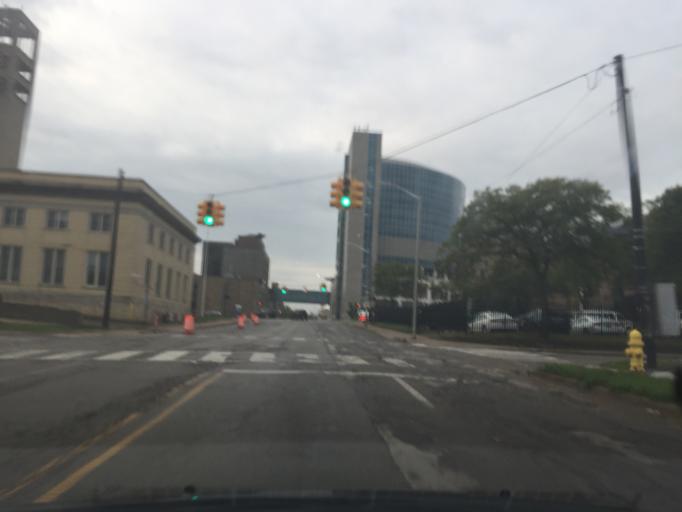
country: US
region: Michigan
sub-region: Oakland County
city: Pontiac
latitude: 42.6401
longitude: -83.2917
